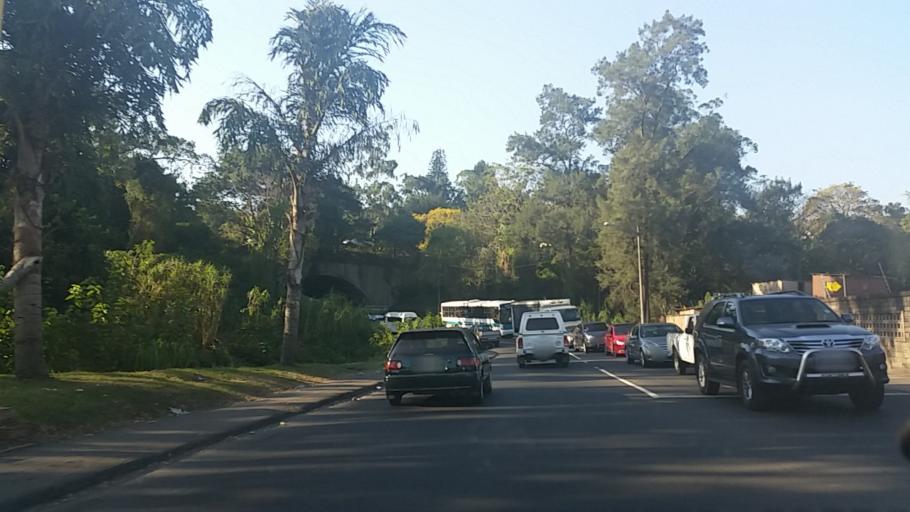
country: ZA
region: KwaZulu-Natal
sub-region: eThekwini Metropolitan Municipality
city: Berea
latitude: -29.8280
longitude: 30.8776
